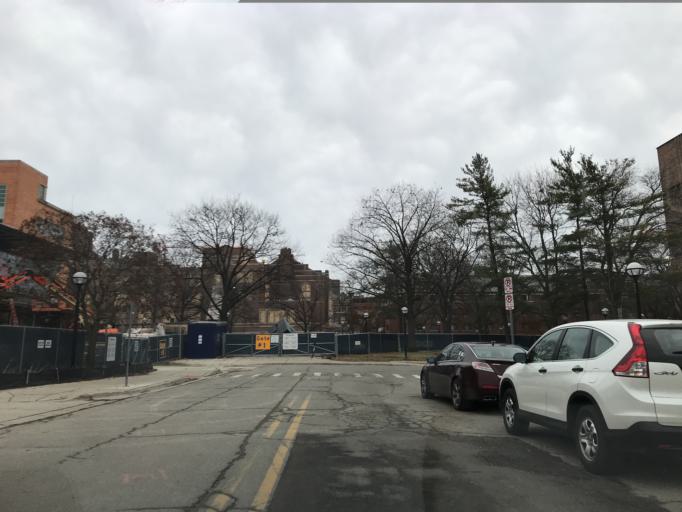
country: US
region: Michigan
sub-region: Washtenaw County
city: Ann Arbor
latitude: 42.2766
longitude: -83.7420
